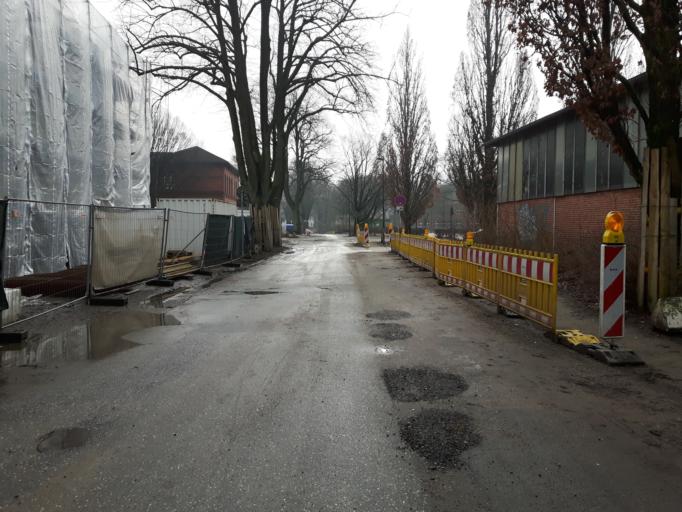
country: DE
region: Schleswig-Holstein
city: Neumunster
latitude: 54.0768
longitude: 9.9895
